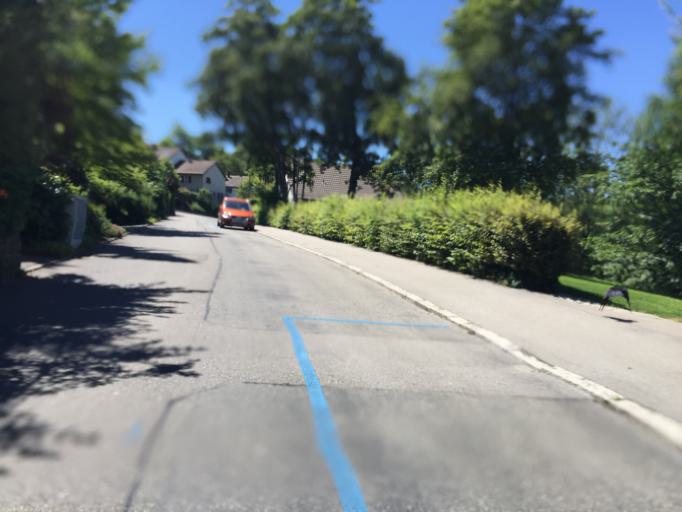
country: CH
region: Bern
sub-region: Bern-Mittelland District
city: Bern
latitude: 46.9648
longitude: 7.4463
